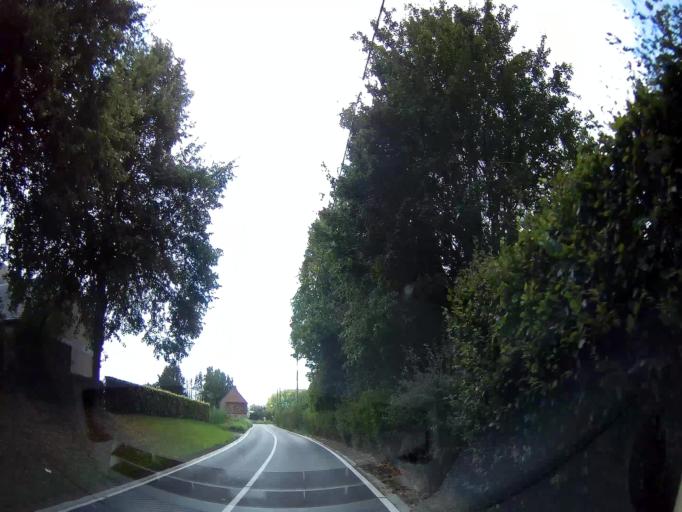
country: BE
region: Wallonia
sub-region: Province de Namur
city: Gesves
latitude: 50.3812
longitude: 5.0708
